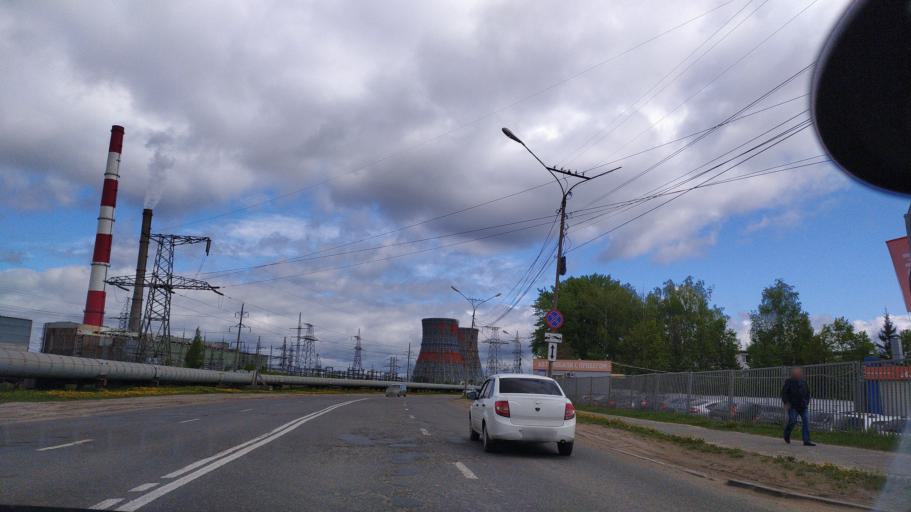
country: RU
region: Chuvashia
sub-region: Cheboksarskiy Rayon
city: Cheboksary
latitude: 56.1193
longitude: 47.3019
